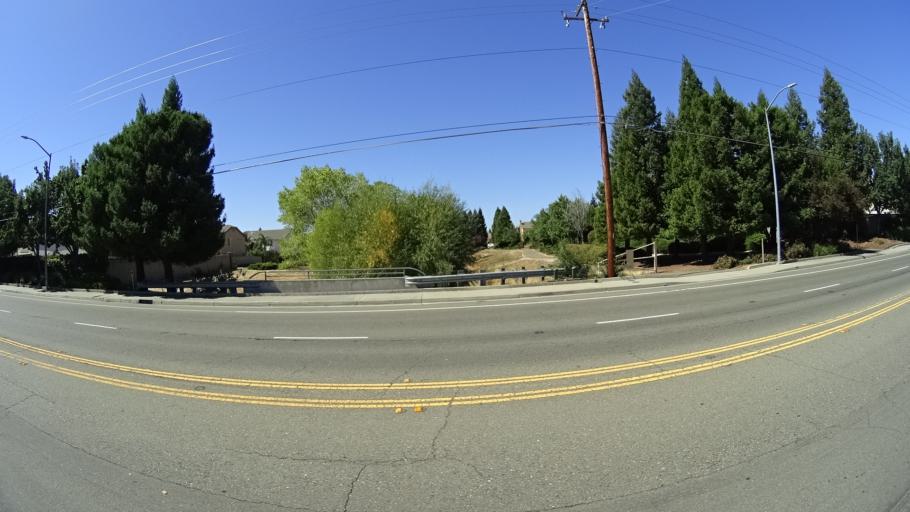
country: US
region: California
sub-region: Sacramento County
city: Elk Grove
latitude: 38.4225
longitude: -121.3347
